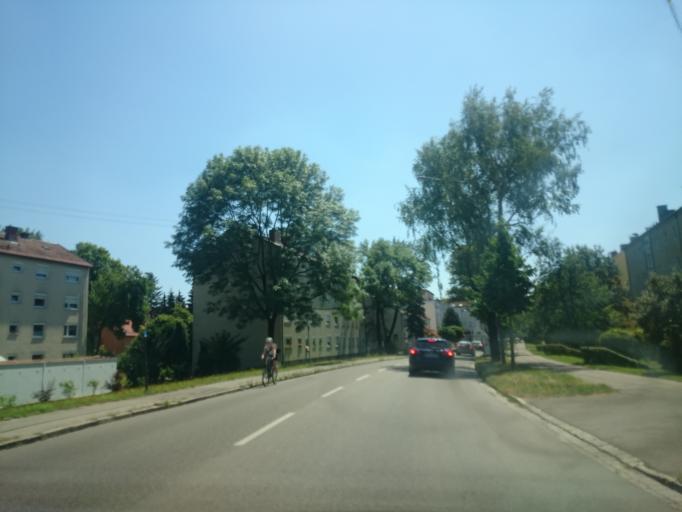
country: DE
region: Bavaria
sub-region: Swabia
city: Stadtbergen
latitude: 48.3519
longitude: 10.8736
